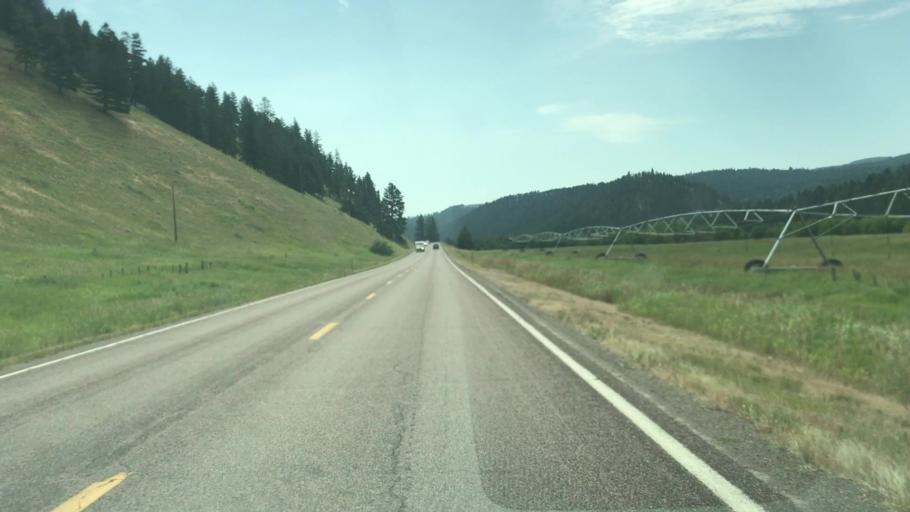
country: US
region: Montana
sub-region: Lewis and Clark County
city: Lincoln
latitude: 46.8153
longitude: -112.8476
